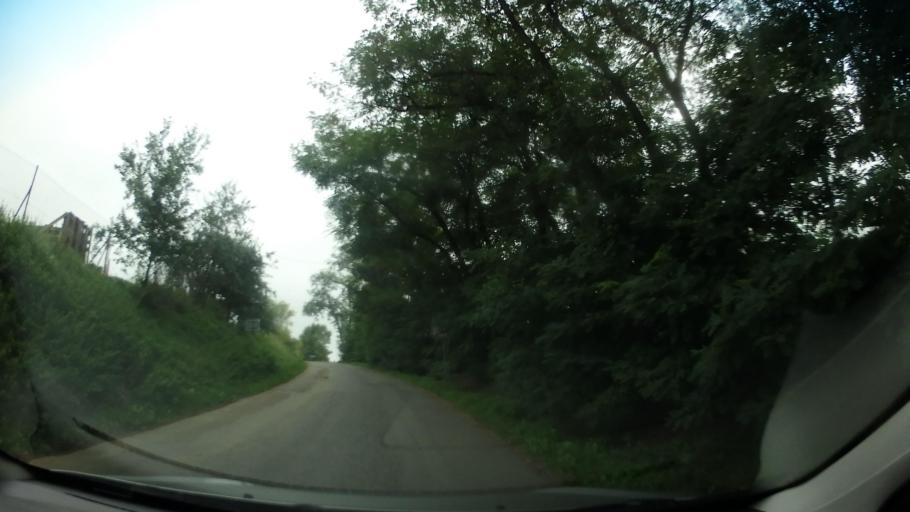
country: CZ
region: Central Bohemia
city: Sedlcany
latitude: 49.7026
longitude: 14.3798
